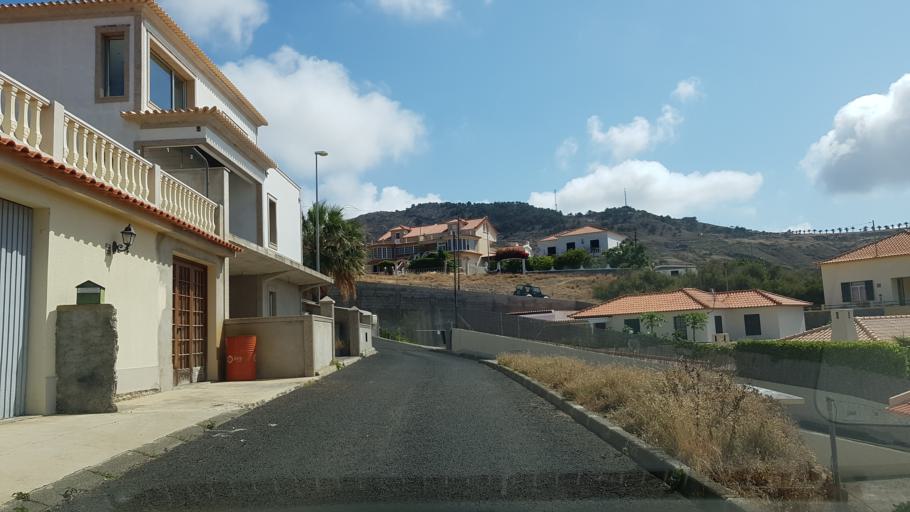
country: PT
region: Madeira
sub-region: Porto Santo
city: Vila de Porto Santo
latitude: 33.0646
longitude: -16.3290
